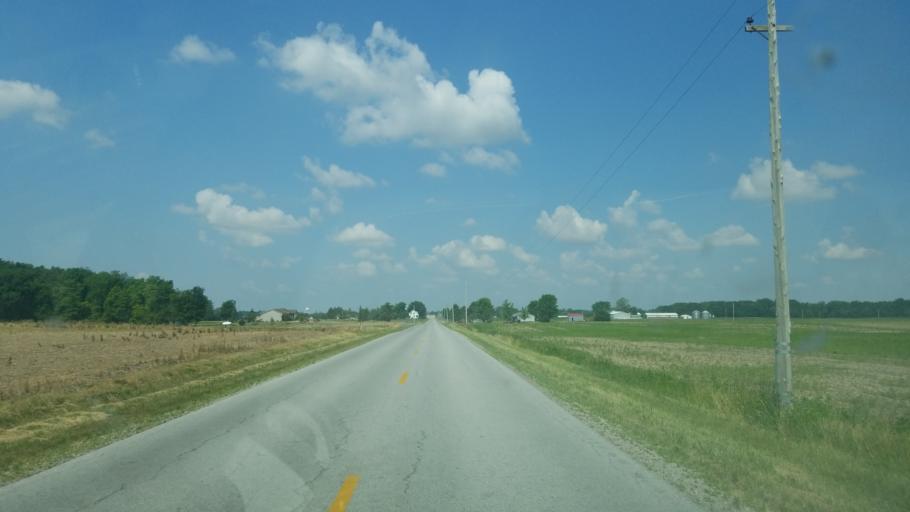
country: US
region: Ohio
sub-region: Auglaize County
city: Wapakoneta
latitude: 40.5702
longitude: -84.1553
